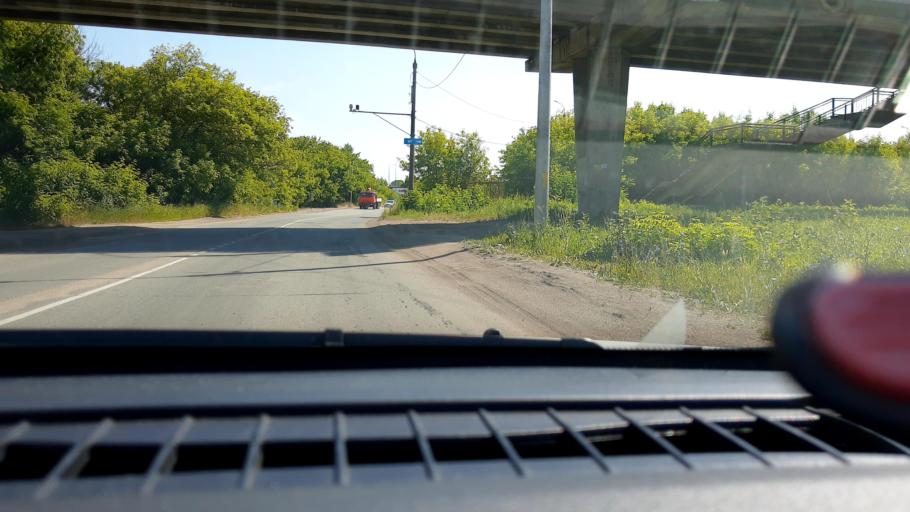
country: RU
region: Nizjnij Novgorod
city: Dzerzhinsk
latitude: 56.2343
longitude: 43.4891
